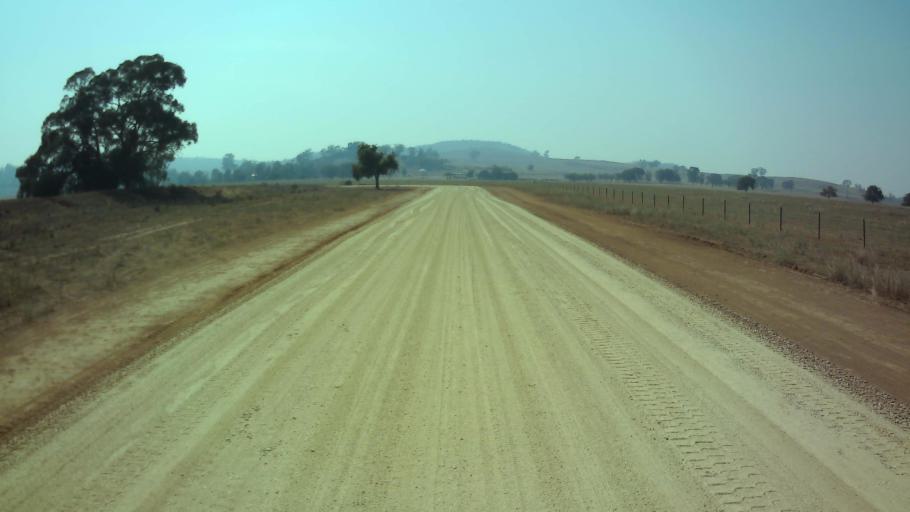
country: AU
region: New South Wales
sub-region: Weddin
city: Grenfell
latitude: -33.8573
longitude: 148.1096
